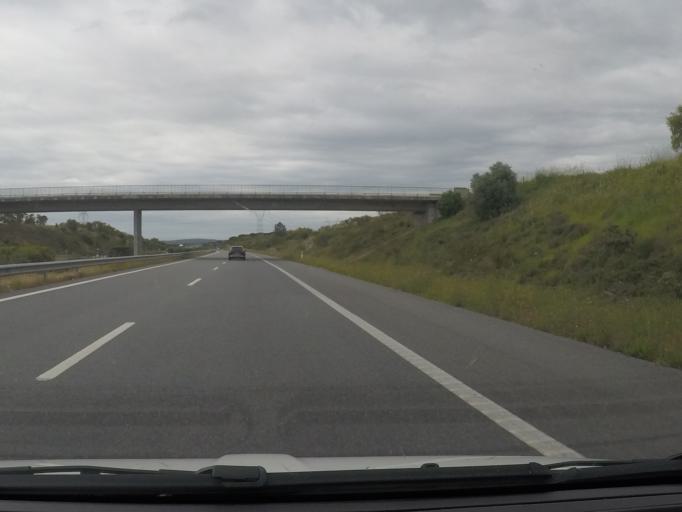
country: PT
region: Setubal
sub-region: Alcacer do Sal
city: Alcacer do Sal
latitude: 38.3977
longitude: -8.4930
